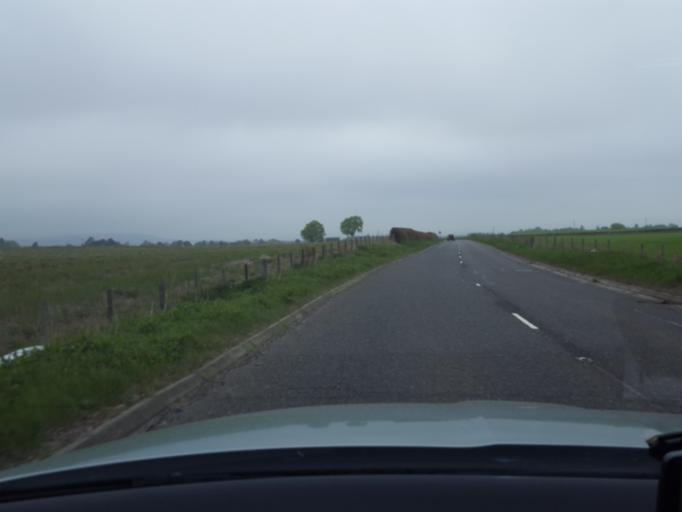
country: GB
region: Scotland
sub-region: Angus
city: Brechin
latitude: 56.7708
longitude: -2.6434
